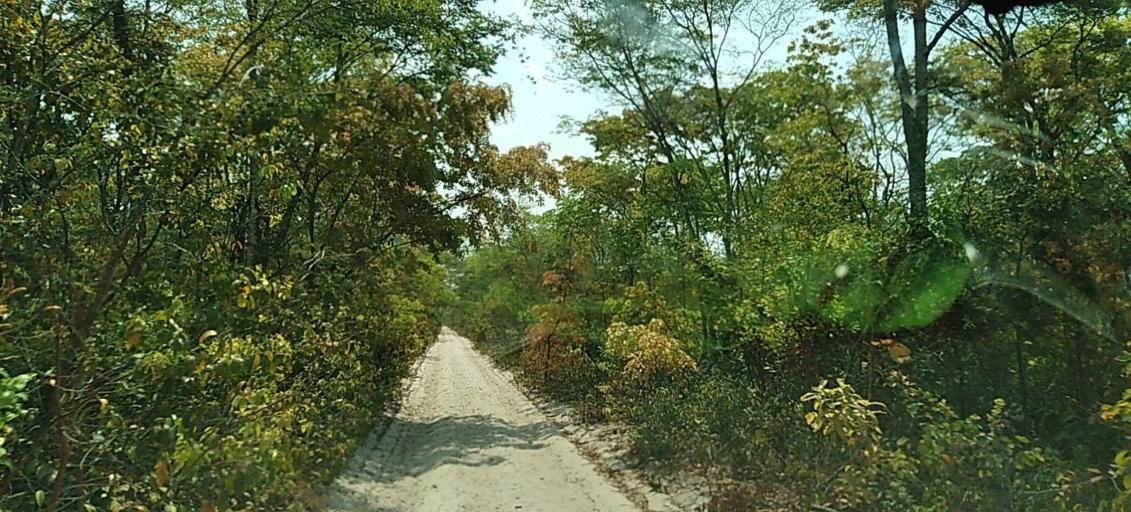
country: ZM
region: North-Western
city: Kabompo
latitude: -13.3954
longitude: 23.7973
